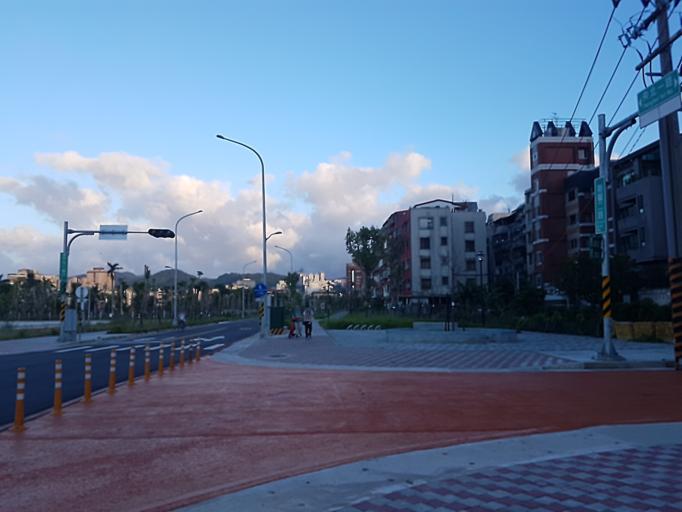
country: TW
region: Taipei
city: Taipei
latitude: 24.9775
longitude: 121.5272
